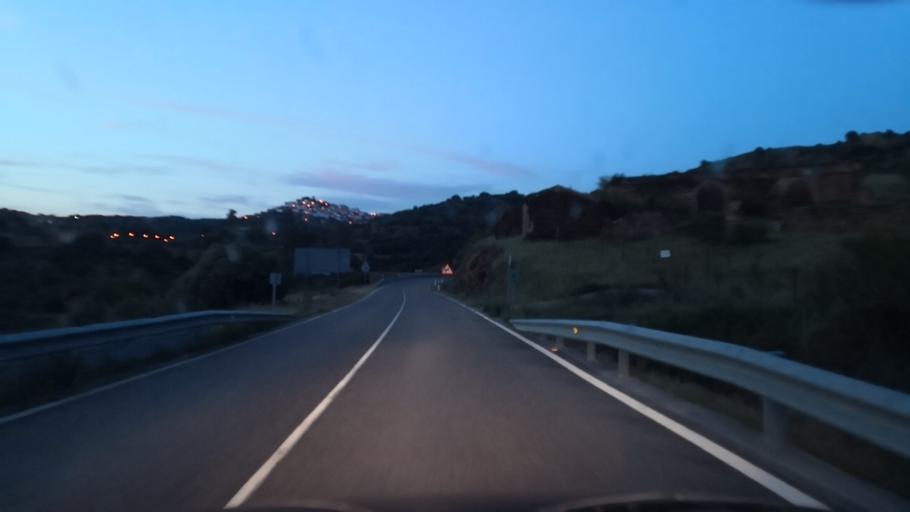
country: ES
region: Extremadura
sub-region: Provincia de Caceres
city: Piedras Albas
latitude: 39.8151
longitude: -6.9829
